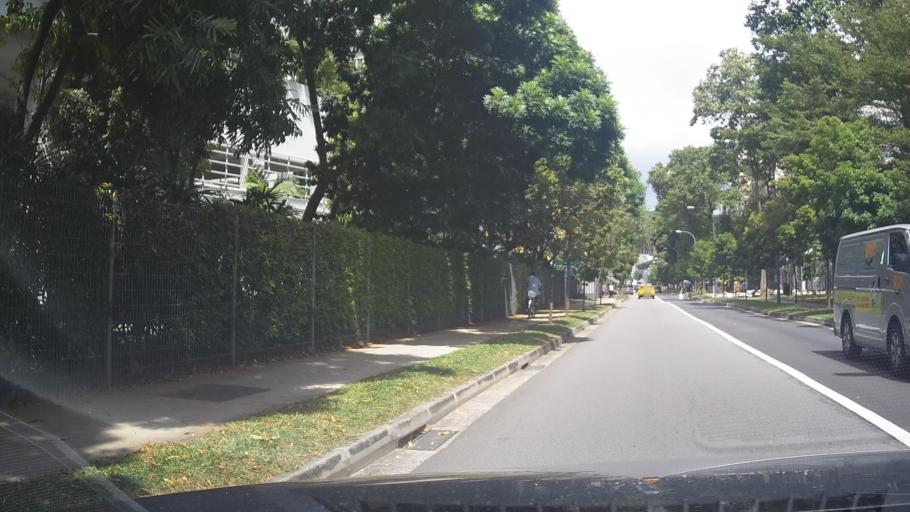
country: SG
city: Singapore
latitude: 1.3123
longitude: 103.8964
